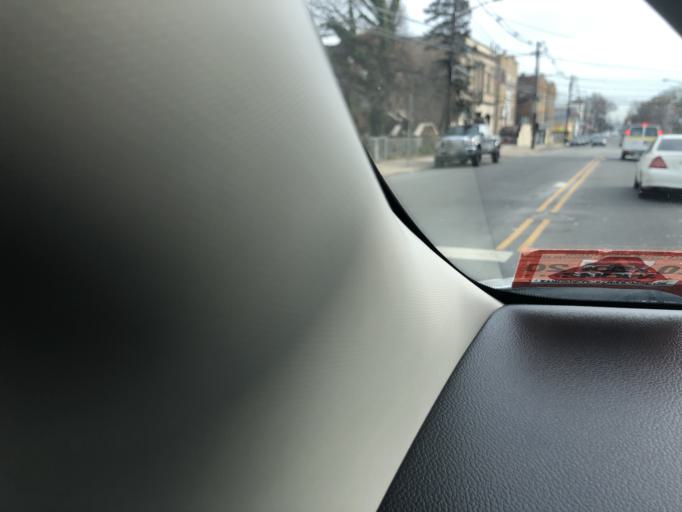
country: US
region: New Jersey
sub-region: Essex County
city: Irvington
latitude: 40.7273
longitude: -74.2092
